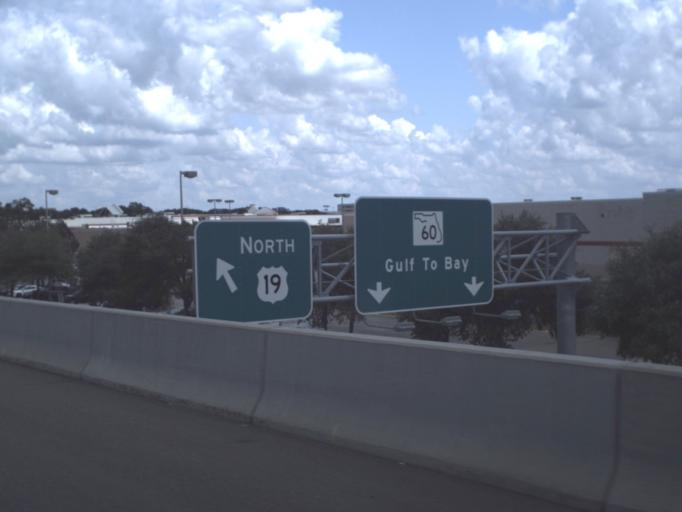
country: US
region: Florida
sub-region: Pinellas County
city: South Highpoint
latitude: 27.9559
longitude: -82.7300
